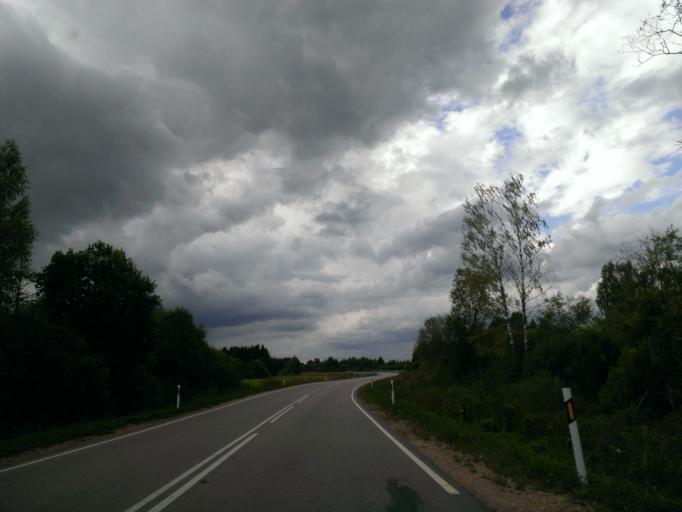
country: LV
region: Malpils
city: Malpils
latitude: 56.8973
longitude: 25.1326
